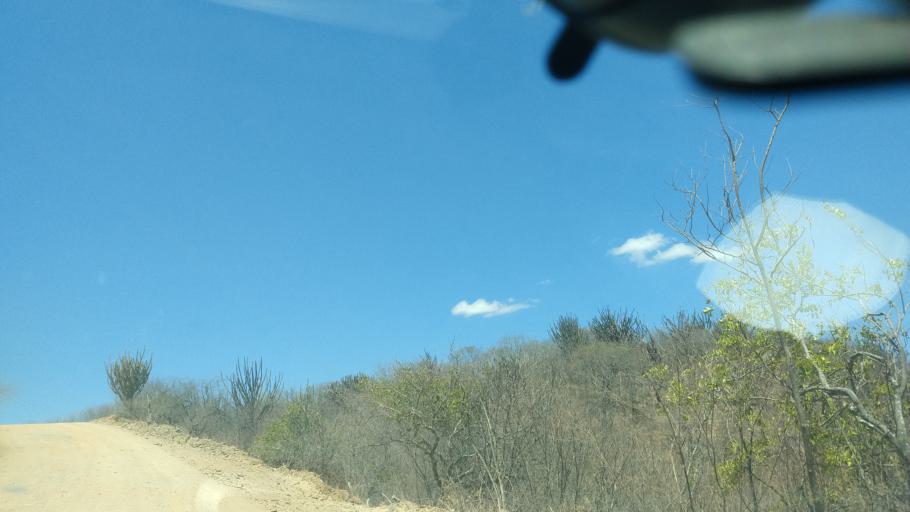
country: BR
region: Rio Grande do Norte
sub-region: Cerro Cora
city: Cerro Cora
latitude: -6.0106
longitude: -36.2786
